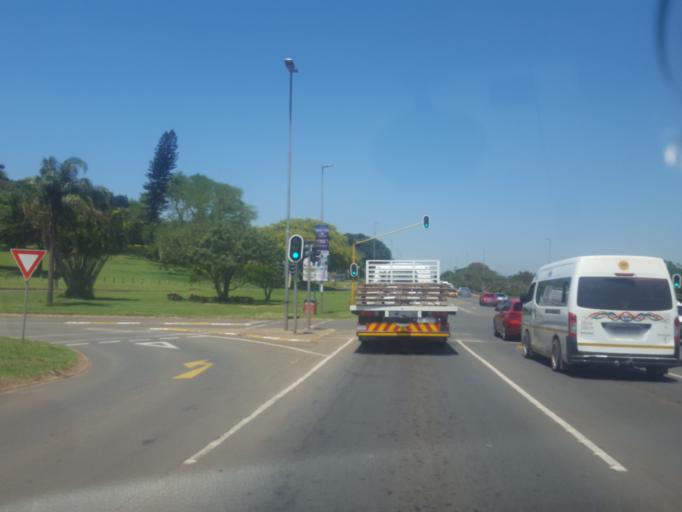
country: ZA
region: KwaZulu-Natal
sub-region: uThungulu District Municipality
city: Empangeni
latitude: -28.7541
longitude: 31.8978
